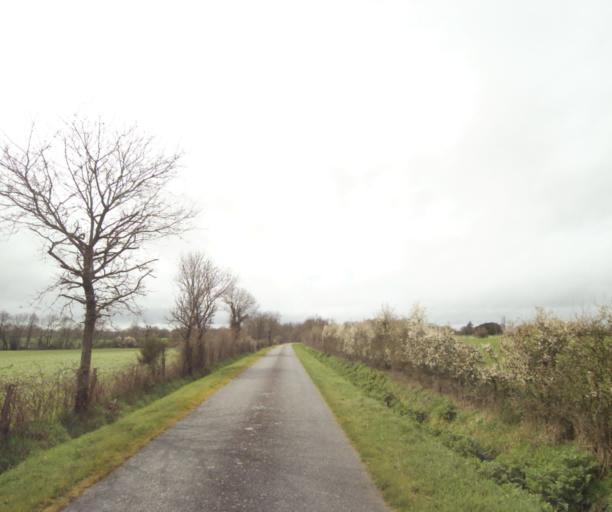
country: FR
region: Pays de la Loire
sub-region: Departement de la Loire-Atlantique
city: Bouvron
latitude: 47.4375
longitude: -1.8641
